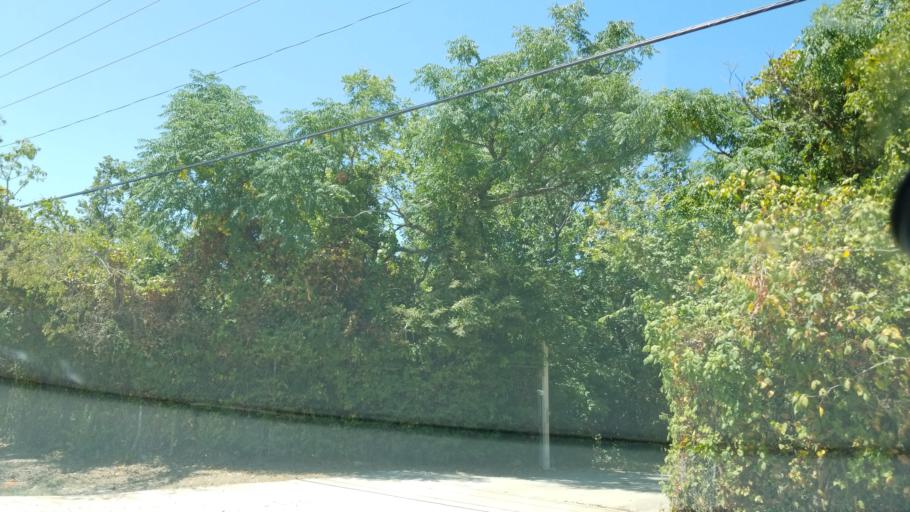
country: US
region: Texas
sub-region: Dallas County
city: Cockrell Hill
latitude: 32.7461
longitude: -96.8914
